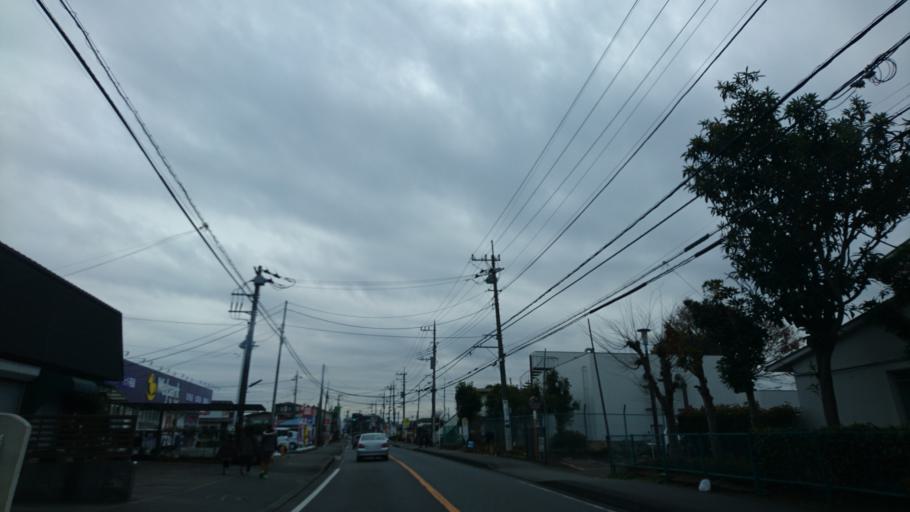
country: JP
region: Tokyo
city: Hachioji
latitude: 35.5766
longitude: 139.3364
